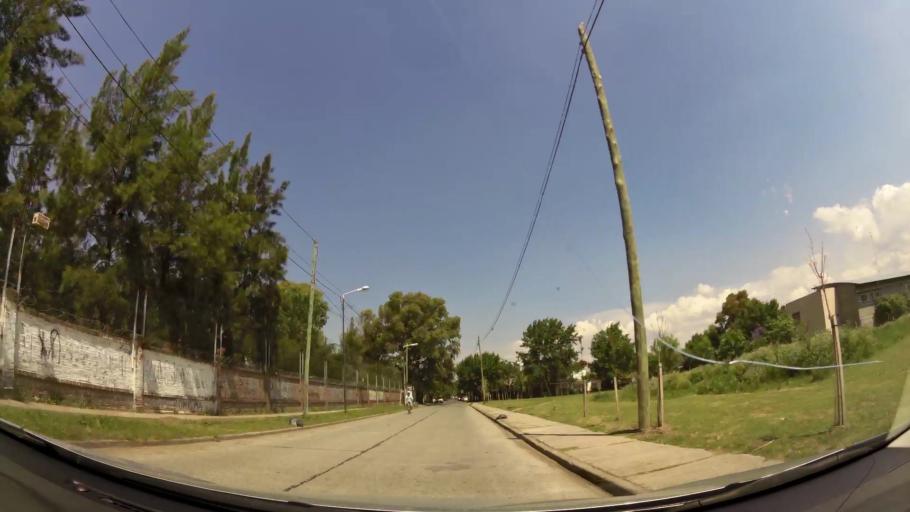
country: AR
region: Buenos Aires
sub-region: Partido de Tigre
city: Tigre
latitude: -34.4628
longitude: -58.5828
